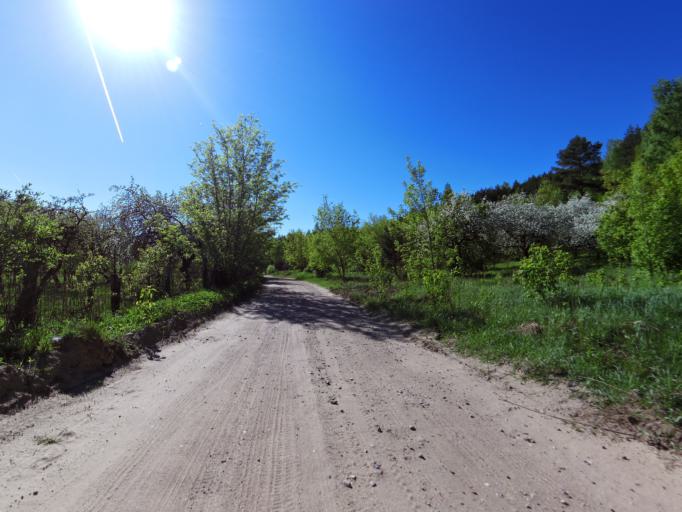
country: LT
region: Vilnius County
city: Pilaite
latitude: 54.6820
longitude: 25.1550
